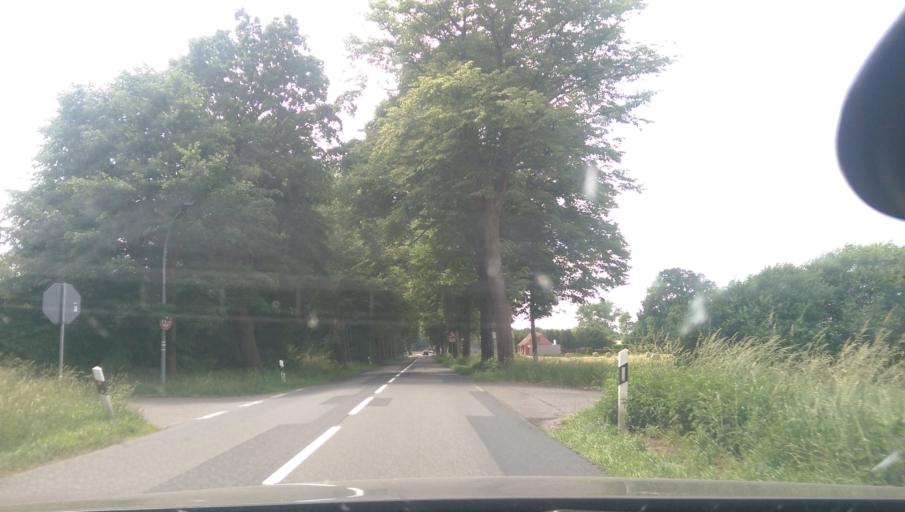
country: DE
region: Lower Saxony
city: Oyten
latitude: 53.0850
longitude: 9.0251
